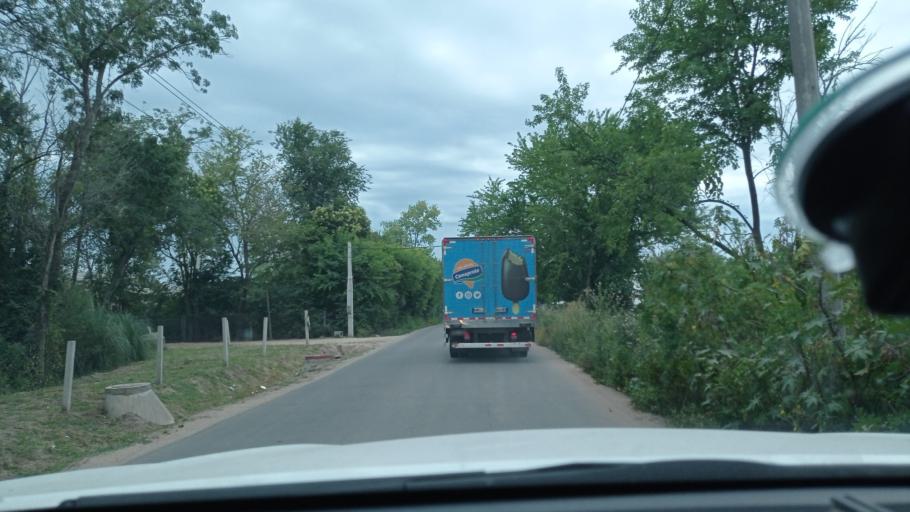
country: UY
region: Canelones
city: La Paz
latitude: -34.8093
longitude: -56.1931
